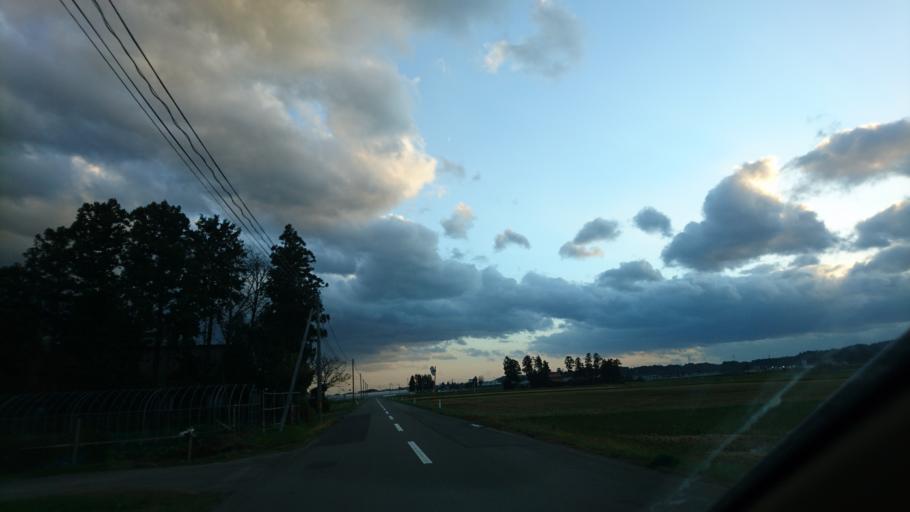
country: JP
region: Iwate
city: Mizusawa
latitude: 39.1094
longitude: 141.1502
